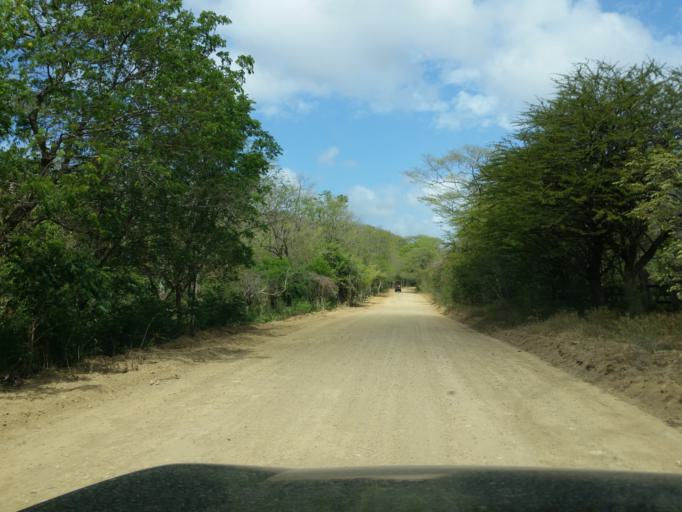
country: NI
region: Rivas
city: San Juan del Sur
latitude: 11.1289
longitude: -85.7802
